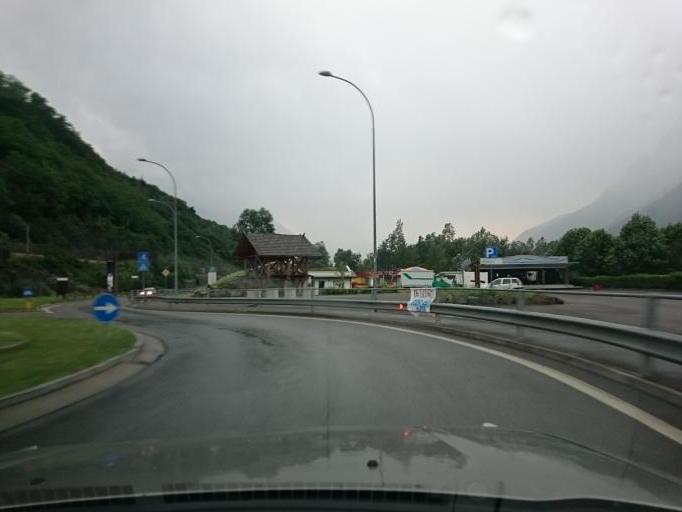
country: IT
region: Lombardy
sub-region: Provincia di Brescia
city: Capo di Ponte
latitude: 46.0272
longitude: 10.3461
